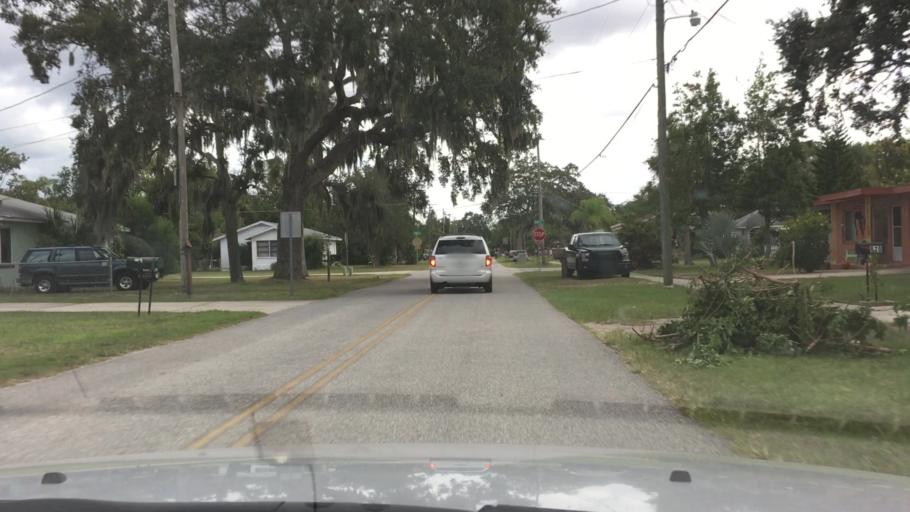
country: US
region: Florida
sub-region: Volusia County
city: Holly Hill
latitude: 29.2407
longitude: -81.0364
